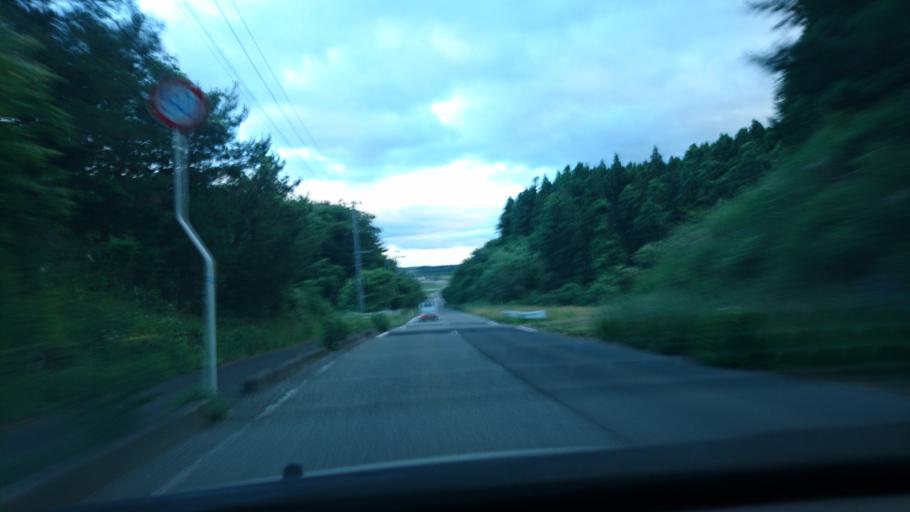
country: JP
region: Iwate
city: Ichinoseki
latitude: 38.7820
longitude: 141.0583
